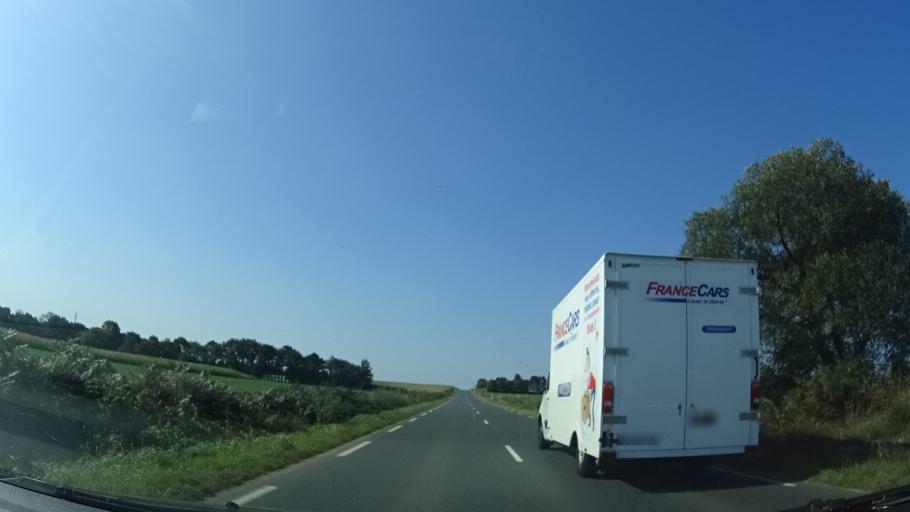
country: FR
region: Brittany
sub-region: Departement du Finistere
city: Cast
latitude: 48.1492
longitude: -4.1477
